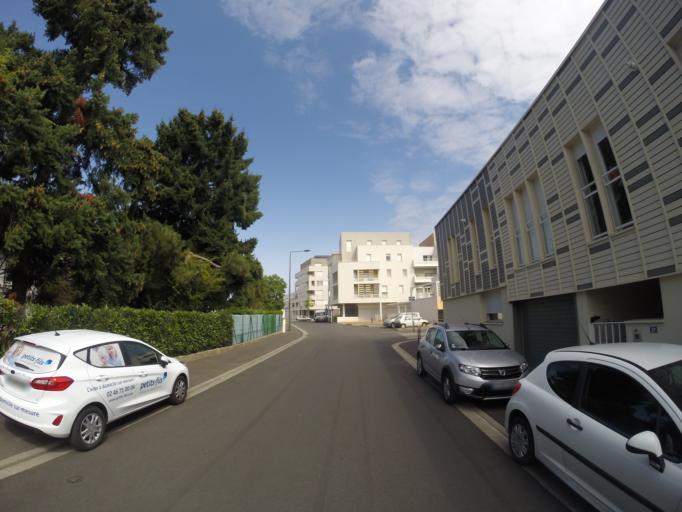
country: FR
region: Centre
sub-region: Departement d'Indre-et-Loire
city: Saint-Cyr-sur-Loire
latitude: 47.4178
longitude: 0.6935
